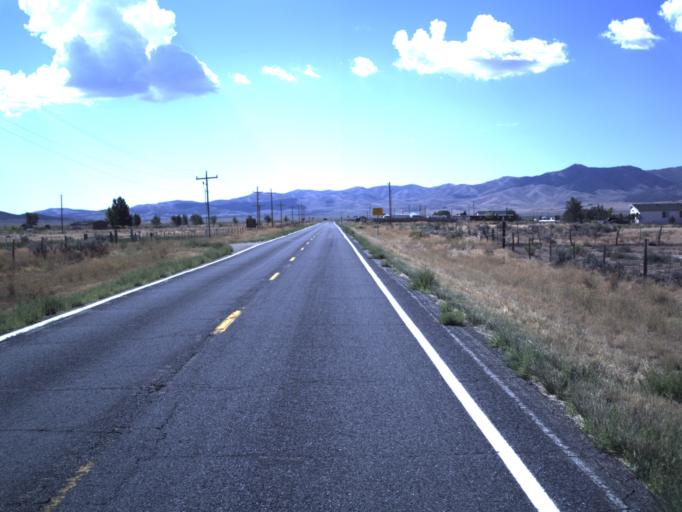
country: US
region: Utah
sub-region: Tooele County
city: Tooele
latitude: 40.0968
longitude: -112.4309
